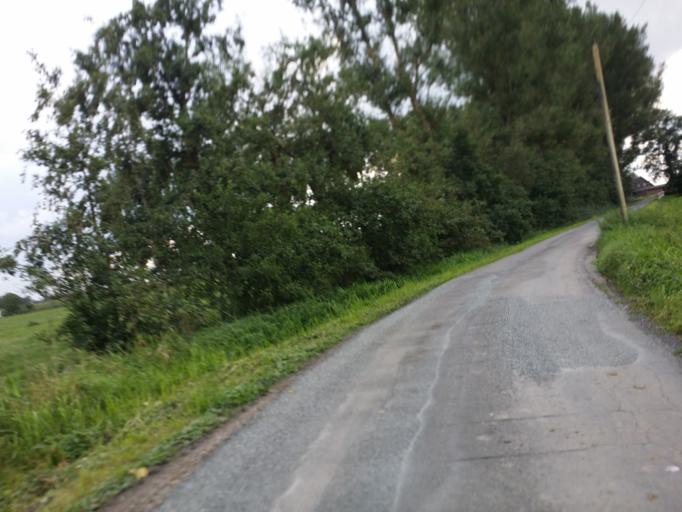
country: DE
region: Lower Saxony
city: Oederquart
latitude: 53.7730
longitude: 9.2162
